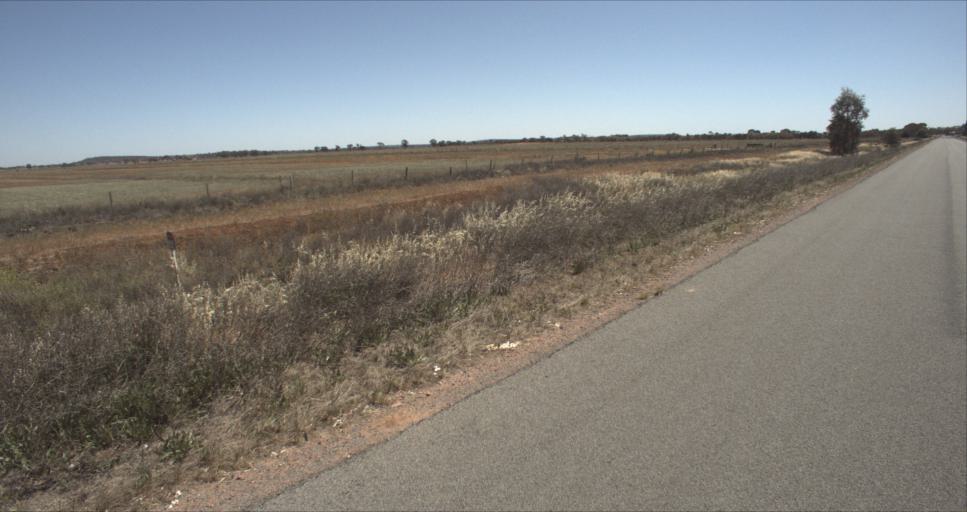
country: AU
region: New South Wales
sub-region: Leeton
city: Leeton
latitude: -34.4368
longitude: 146.2986
